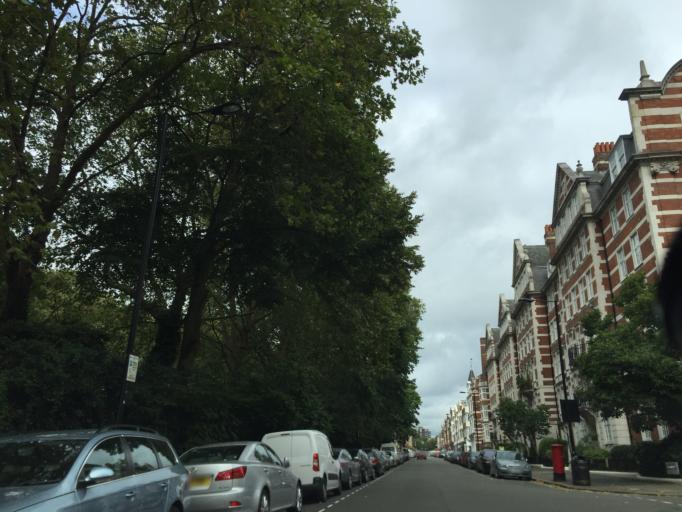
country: GB
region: England
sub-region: Greater London
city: Belsize Park
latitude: 51.5313
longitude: -0.1680
